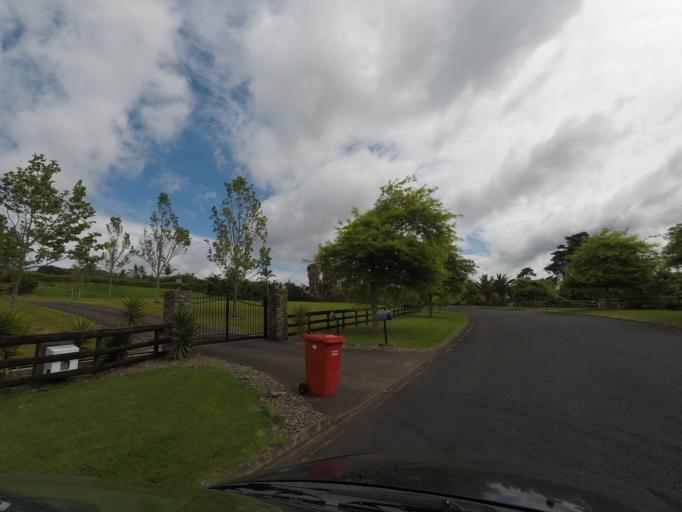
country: NZ
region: Auckland
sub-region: Auckland
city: Muriwai Beach
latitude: -36.7664
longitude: 174.5709
